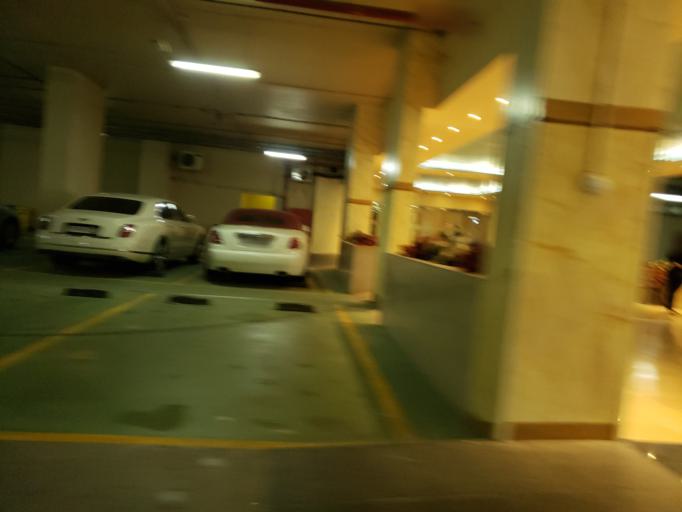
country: AE
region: Dubai
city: Dubai
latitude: 25.1032
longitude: 55.1720
